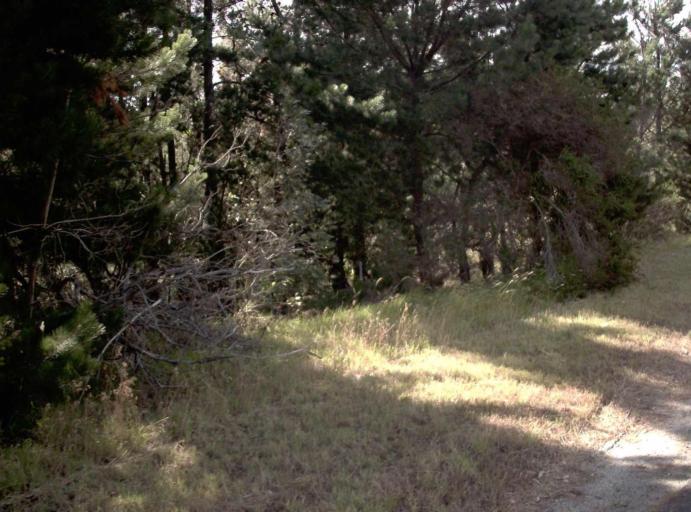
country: AU
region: Victoria
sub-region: Latrobe
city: Morwell
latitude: -38.1842
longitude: 146.4042
